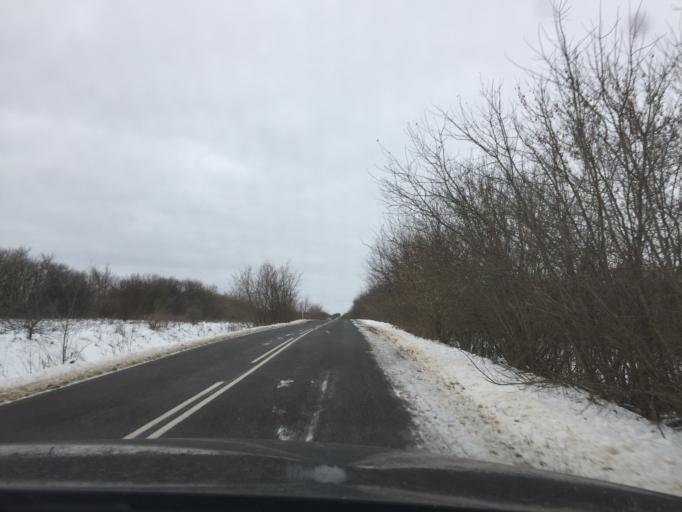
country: RU
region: Tula
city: Teploye
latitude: 53.7917
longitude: 37.6075
